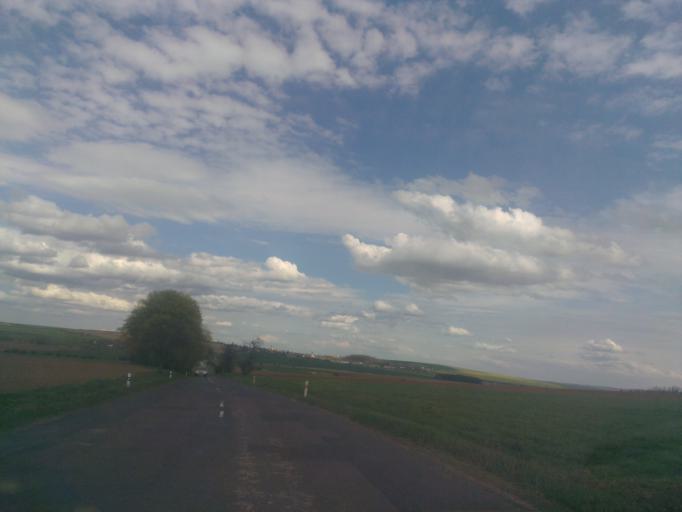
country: CZ
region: South Moravian
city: Dolni Kounice
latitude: 49.1060
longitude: 16.4786
